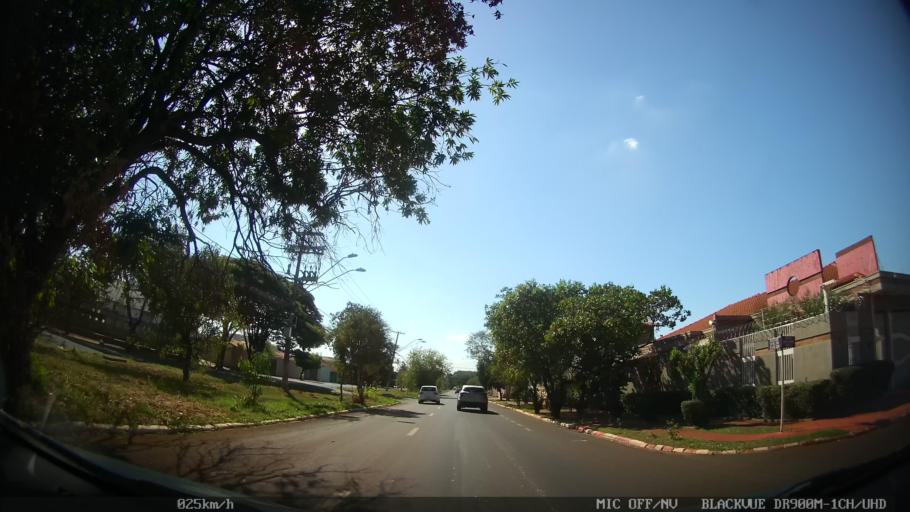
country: BR
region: Sao Paulo
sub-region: Ribeirao Preto
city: Ribeirao Preto
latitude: -21.1908
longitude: -47.7609
